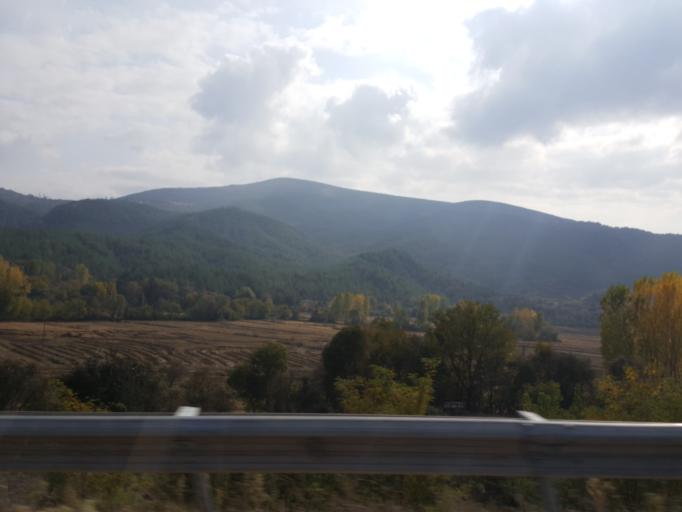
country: TR
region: Sinop
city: Sarayduzu
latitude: 41.3852
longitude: 34.9201
